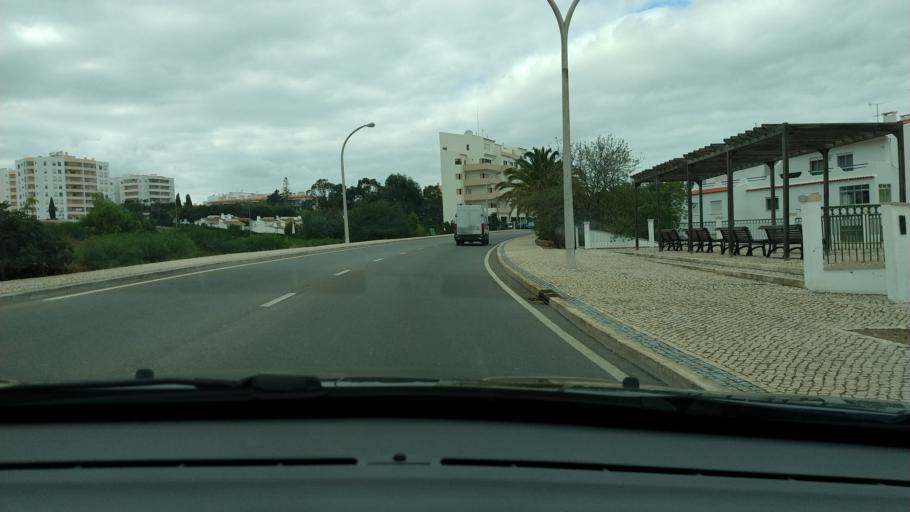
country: PT
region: Faro
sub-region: Lagos
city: Lagos
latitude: 37.0958
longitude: -8.6770
